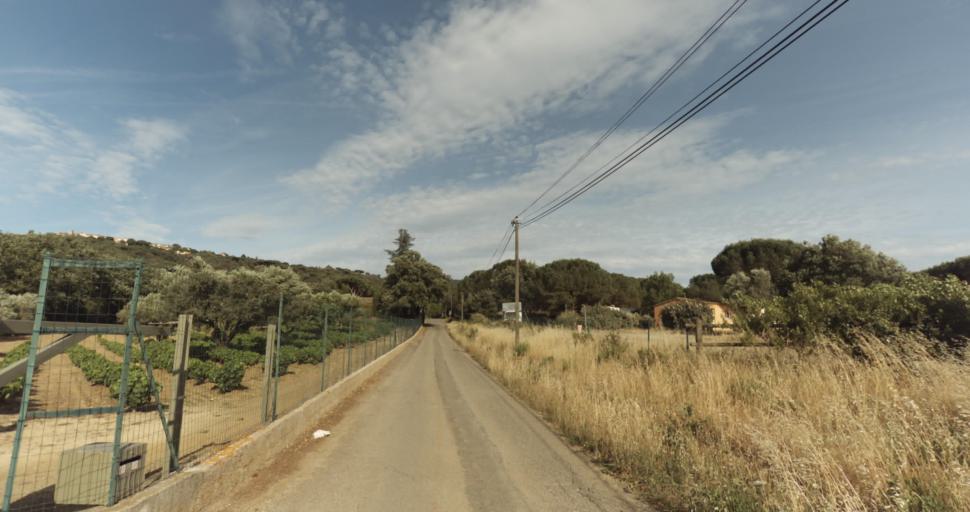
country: FR
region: Provence-Alpes-Cote d'Azur
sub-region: Departement du Var
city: Gassin
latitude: 43.2260
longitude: 6.5741
